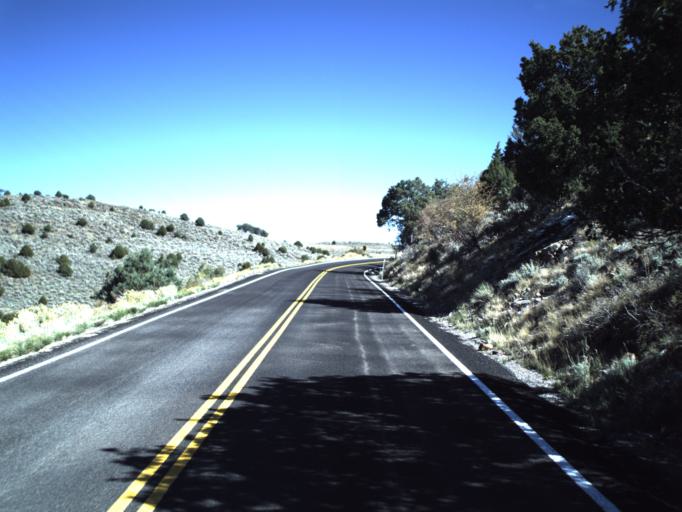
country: US
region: Utah
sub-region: Wayne County
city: Loa
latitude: 38.4906
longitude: -111.8158
